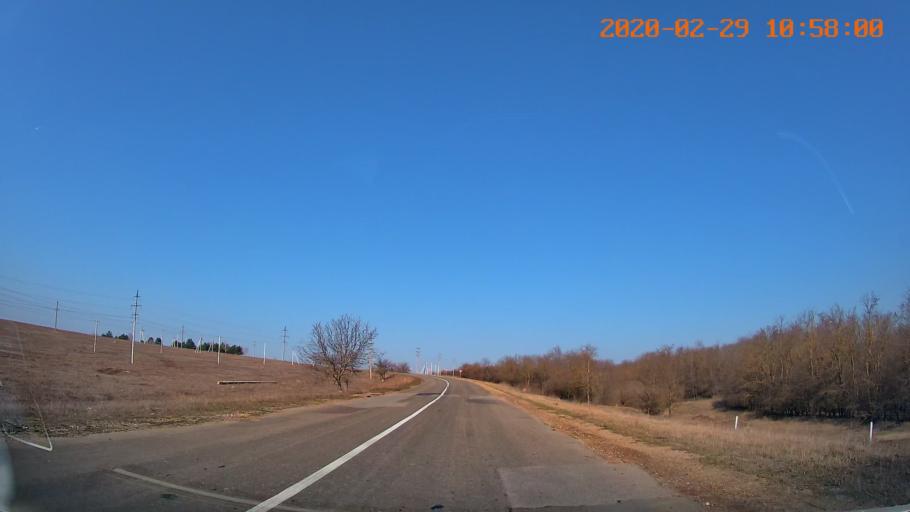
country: MD
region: Telenesti
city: Grigoriopol
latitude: 47.1657
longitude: 29.3180
